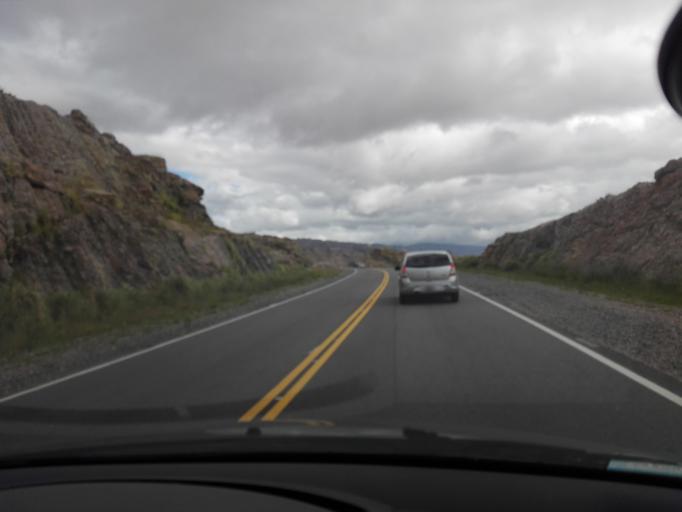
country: AR
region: Cordoba
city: Mina Clavero
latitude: -31.6380
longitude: -64.9076
